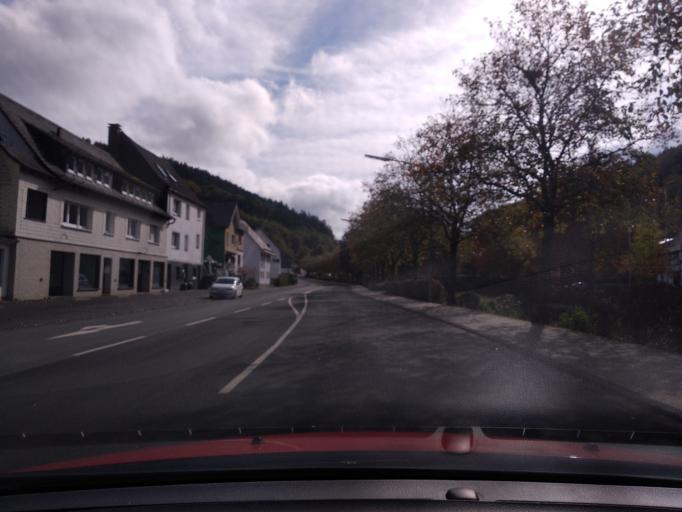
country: DE
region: North Rhine-Westphalia
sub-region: Regierungsbezirk Arnsberg
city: Bestwig
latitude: 51.3087
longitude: 8.4022
